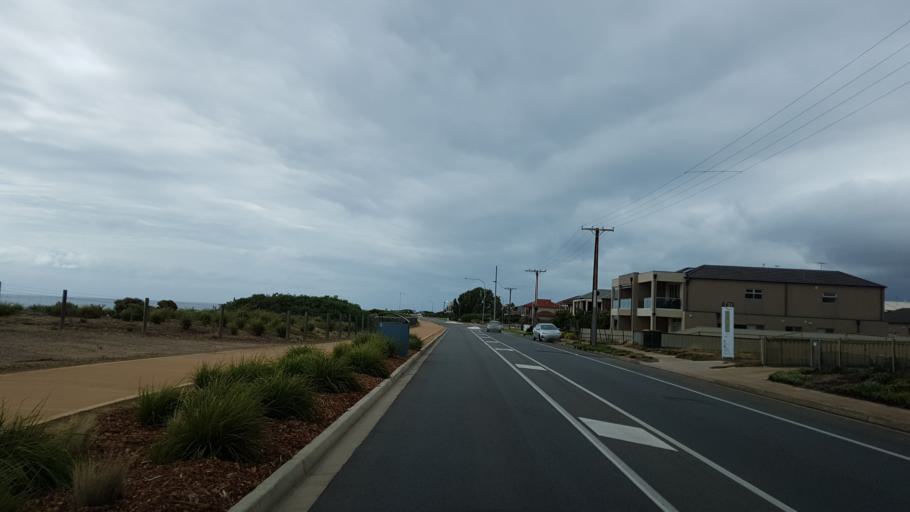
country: AU
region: South Australia
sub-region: Onkaparinga
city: Port Willunga
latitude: -35.2806
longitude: 138.4439
